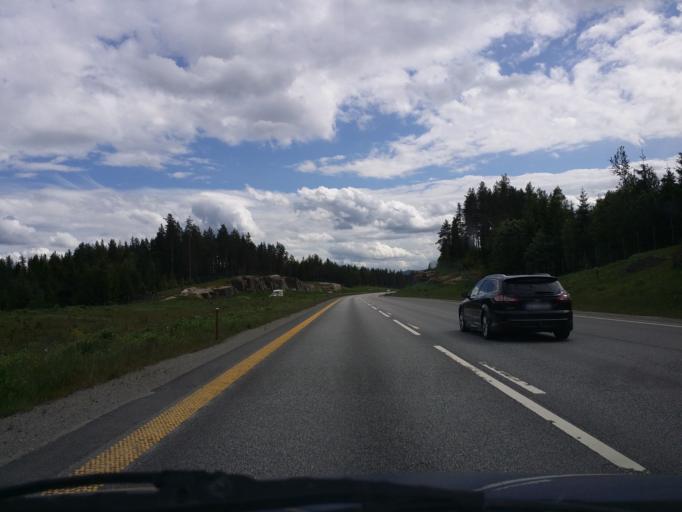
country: NO
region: Hedmark
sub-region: Stange
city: Stange
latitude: 60.6888
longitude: 11.2799
